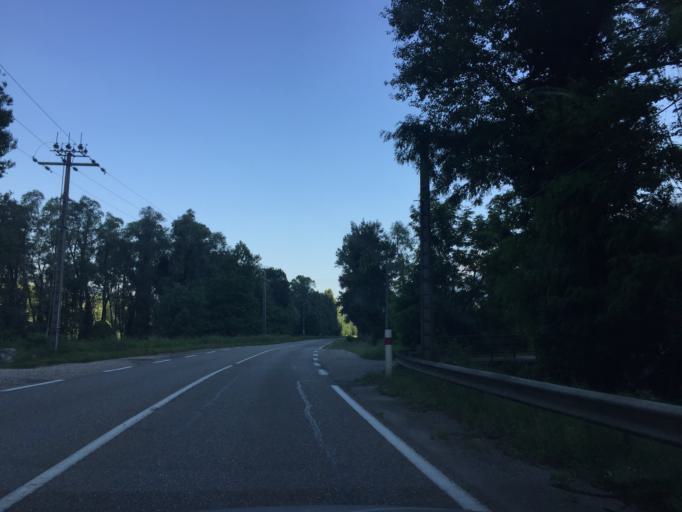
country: FR
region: Rhone-Alpes
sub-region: Departement de l'Isere
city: Voreppe
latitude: 45.2949
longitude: 5.6137
